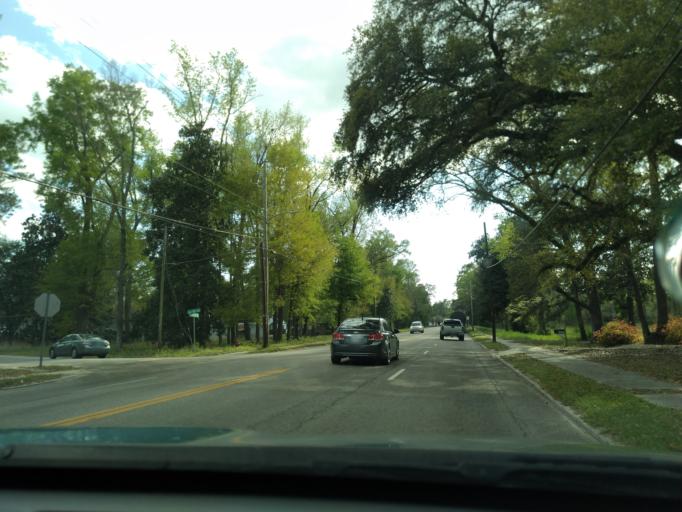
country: US
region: South Carolina
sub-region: Williamsburg County
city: Kingstree
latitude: 33.6760
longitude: -79.8327
